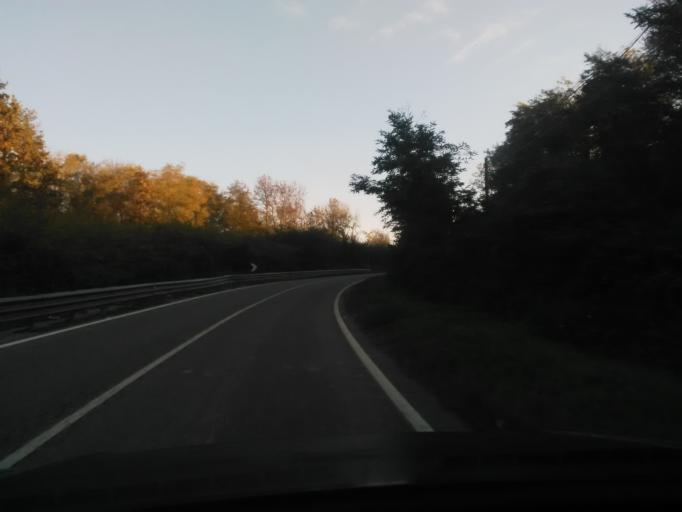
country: IT
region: Piedmont
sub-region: Provincia di Vercelli
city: Carisio
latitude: 45.4004
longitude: 8.1881
